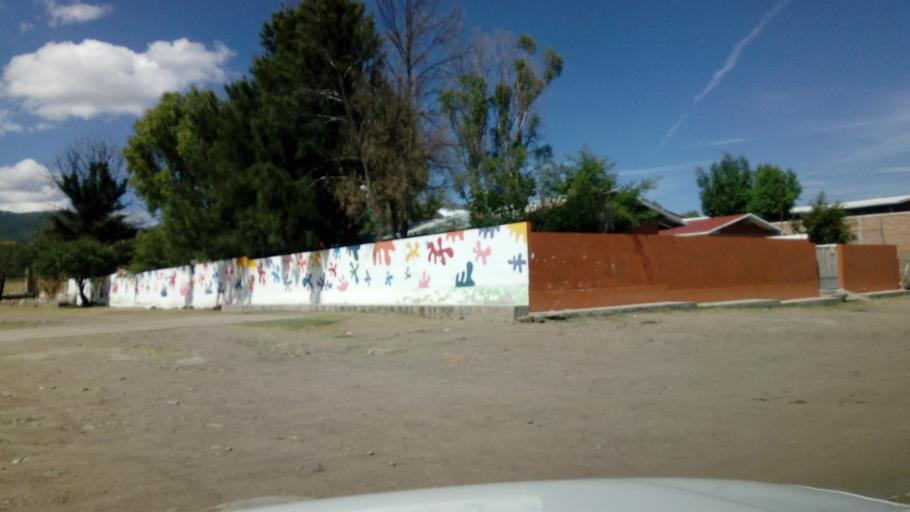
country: MX
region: Durango
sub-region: Durango
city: Jose Refugio Salcido
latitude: 23.7911
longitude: -104.4876
